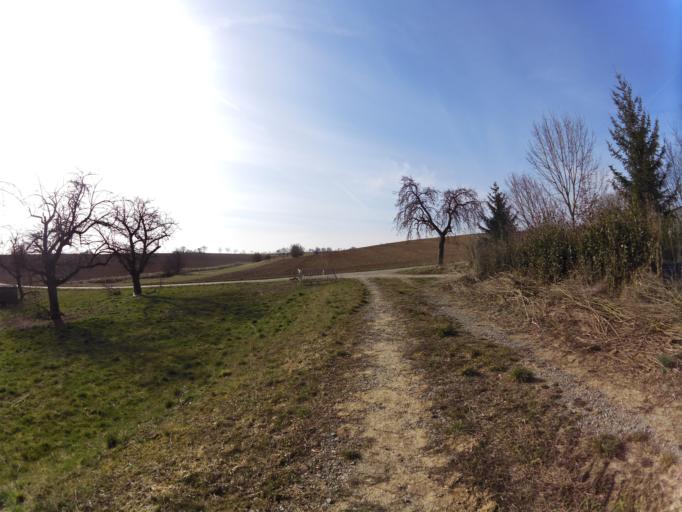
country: DE
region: Bavaria
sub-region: Regierungsbezirk Unterfranken
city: Prosselsheim
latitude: 49.8285
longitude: 10.1186
